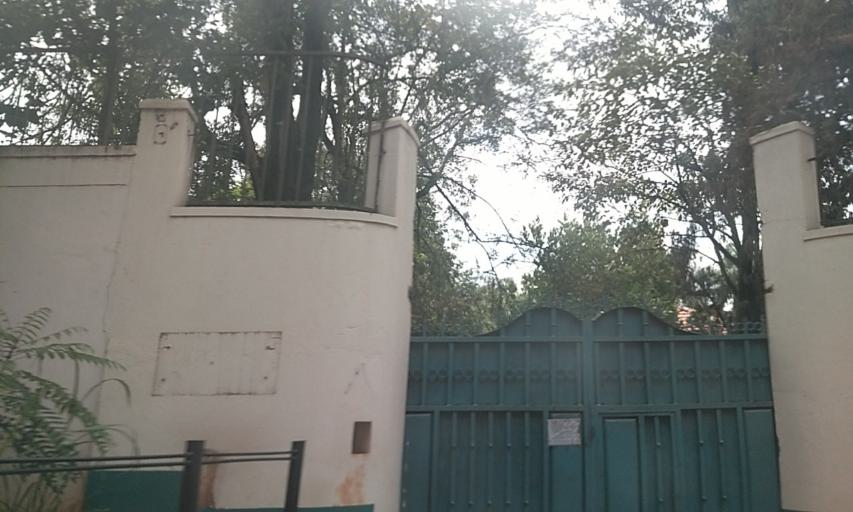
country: UG
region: Central Region
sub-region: Kampala District
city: Kampala
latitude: 0.3276
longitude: 32.5903
